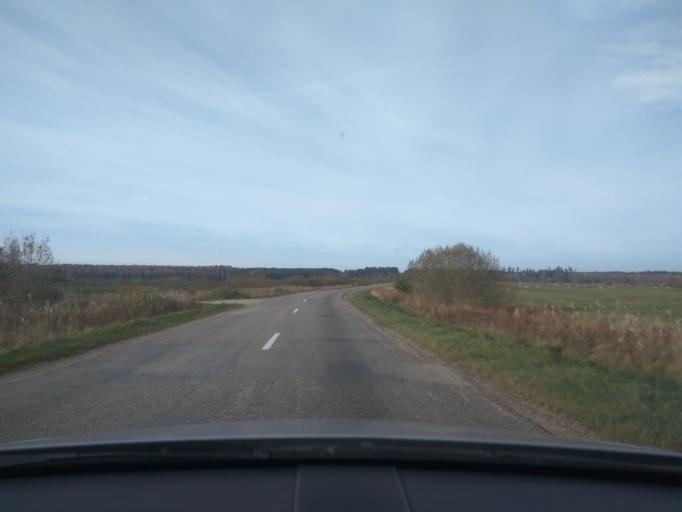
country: LV
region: Alsunga
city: Alsunga
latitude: 56.9847
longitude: 21.5350
